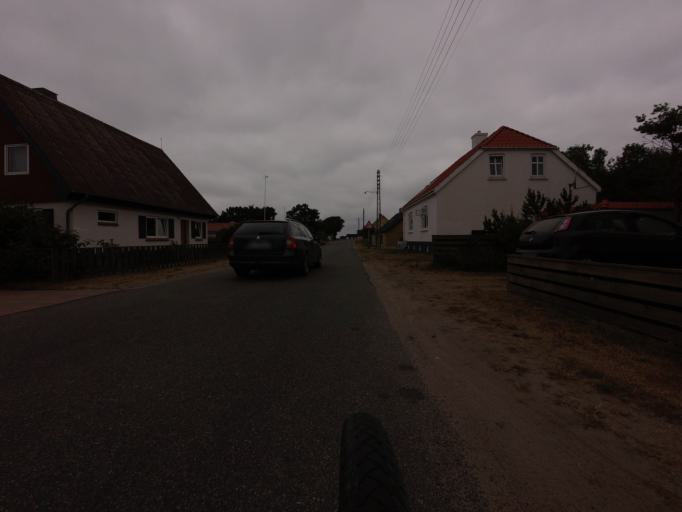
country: DK
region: North Denmark
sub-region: Laeso Kommune
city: Byrum
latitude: 57.2949
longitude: 10.9259
